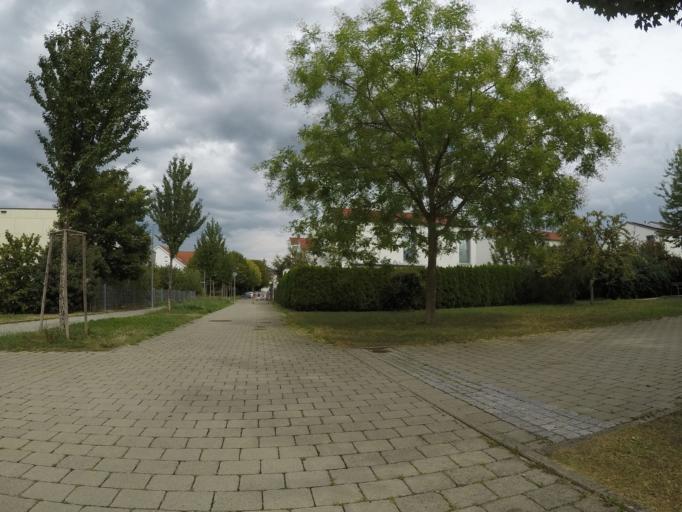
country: DE
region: Baden-Wuerttemberg
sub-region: Tuebingen Region
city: Reutlingen
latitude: 48.4802
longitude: 9.2049
